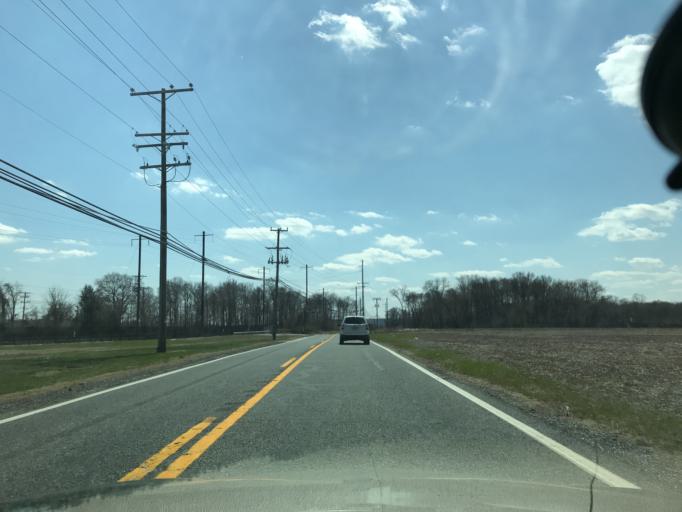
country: US
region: Maryland
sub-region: Harford County
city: Perryman
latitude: 39.4581
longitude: -76.2093
